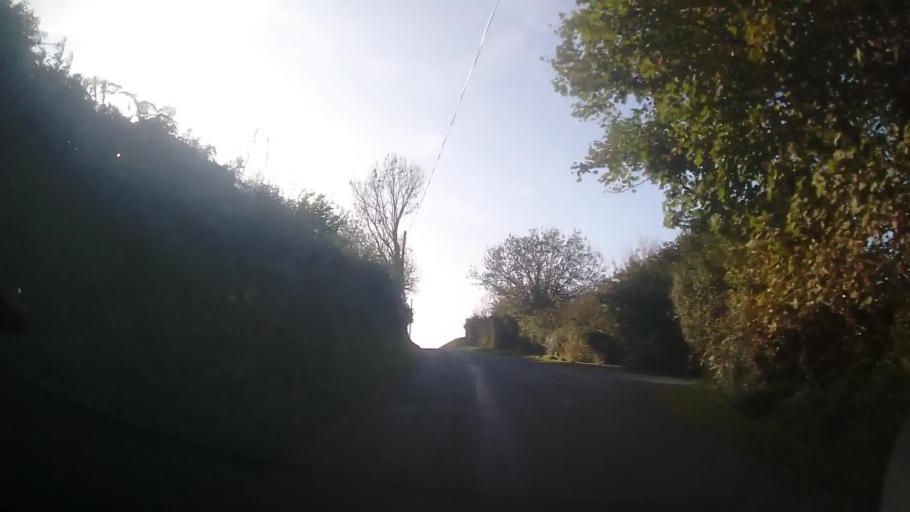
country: GB
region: Wales
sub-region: Pembrokeshire
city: Fishguard
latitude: 51.9826
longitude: -4.9439
